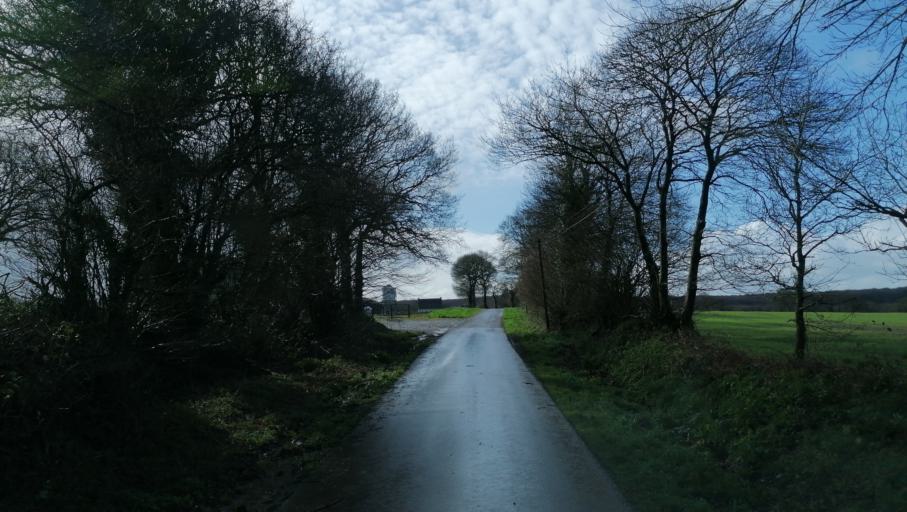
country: FR
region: Brittany
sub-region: Departement des Cotes-d'Armor
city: Lanrodec
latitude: 48.4890
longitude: -3.0266
